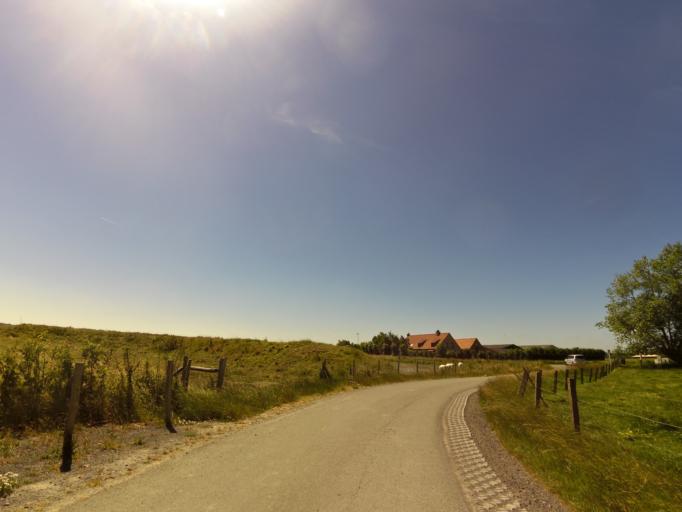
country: NL
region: Zeeland
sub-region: Gemeente Sluis
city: Sluis
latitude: 51.3343
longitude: 3.3648
